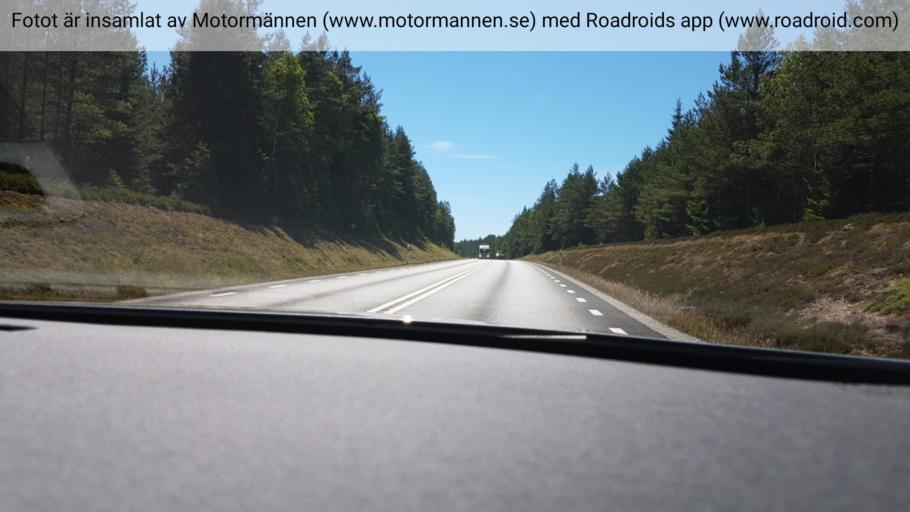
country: SE
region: Joenkoeping
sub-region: Gnosjo Kommun
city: Gnosjoe
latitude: 57.5675
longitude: 13.7050
